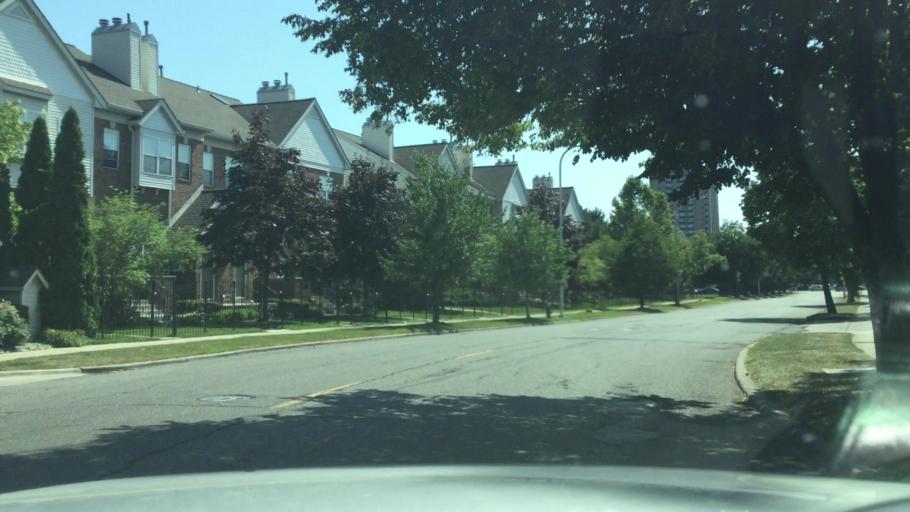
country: US
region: Michigan
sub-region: Wayne County
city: Detroit
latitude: 42.3483
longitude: -83.0238
